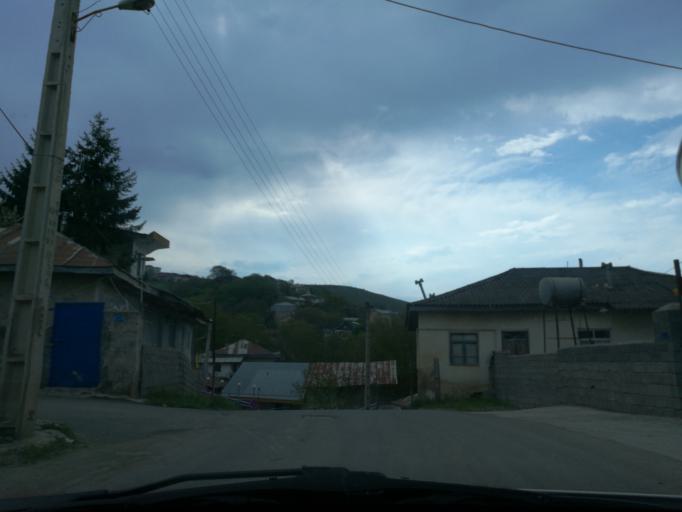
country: IR
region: Mazandaran
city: Chalus
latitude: 36.5315
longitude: 51.2269
